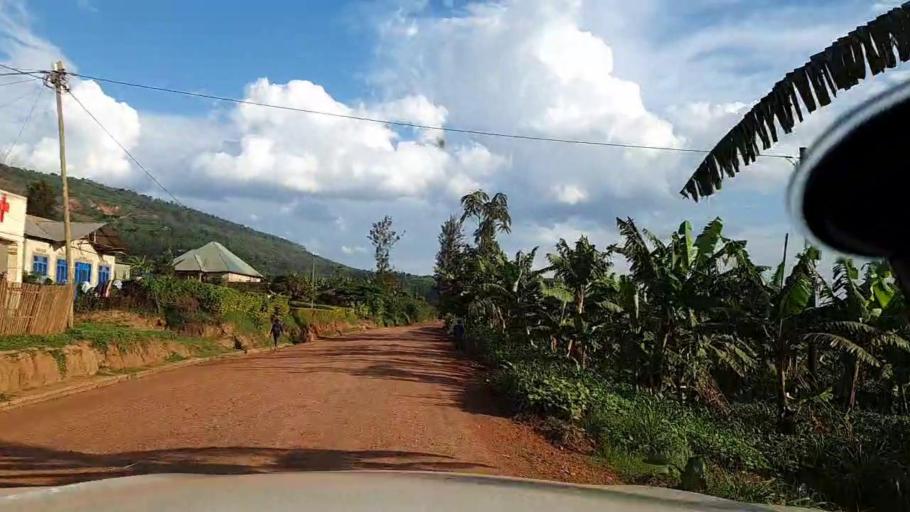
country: RW
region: Kigali
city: Kigali
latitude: -1.9135
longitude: 29.9853
